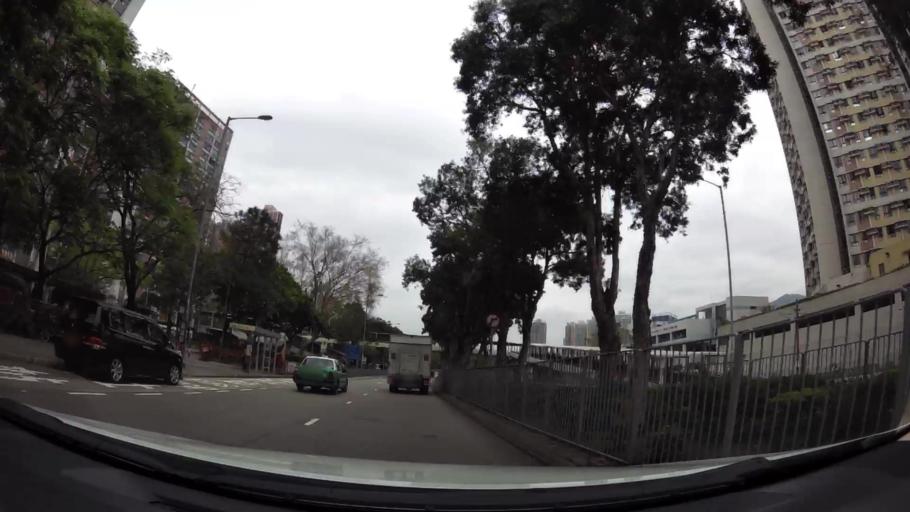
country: HK
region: Tuen Mun
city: Tuen Mun
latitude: 22.3767
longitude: 113.9663
